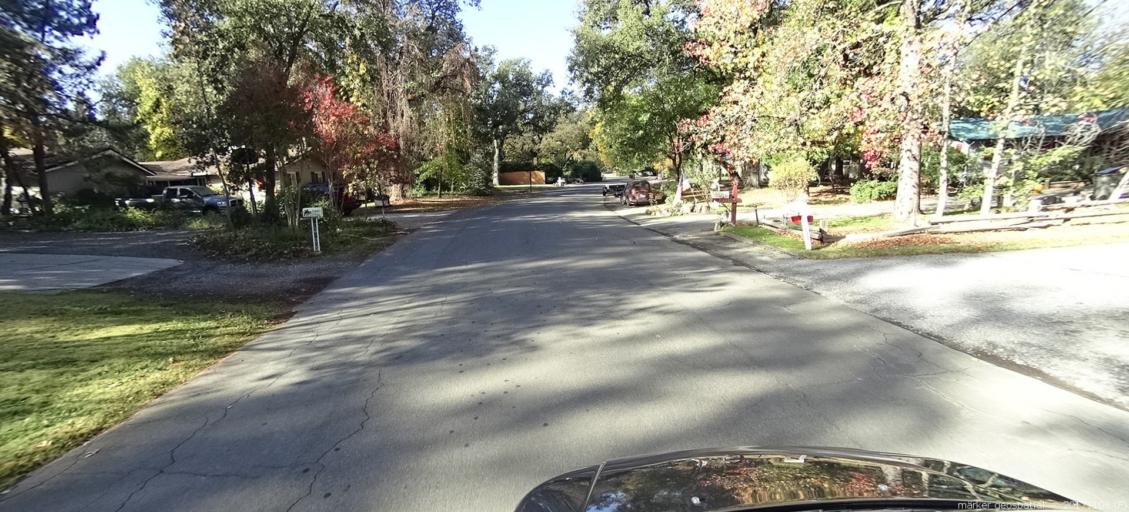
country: US
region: California
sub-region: Shasta County
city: Palo Cedro
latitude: 40.5417
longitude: -122.2451
